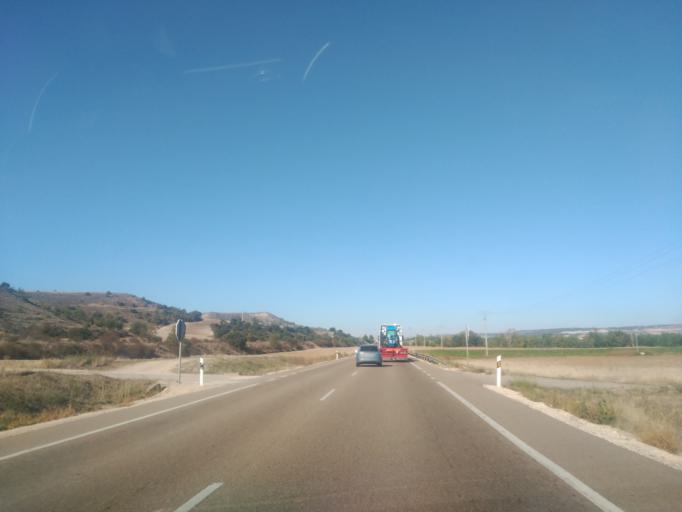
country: ES
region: Castille and Leon
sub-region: Provincia de Valladolid
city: Quintanilla de Arriba
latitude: 41.6219
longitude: -4.2437
